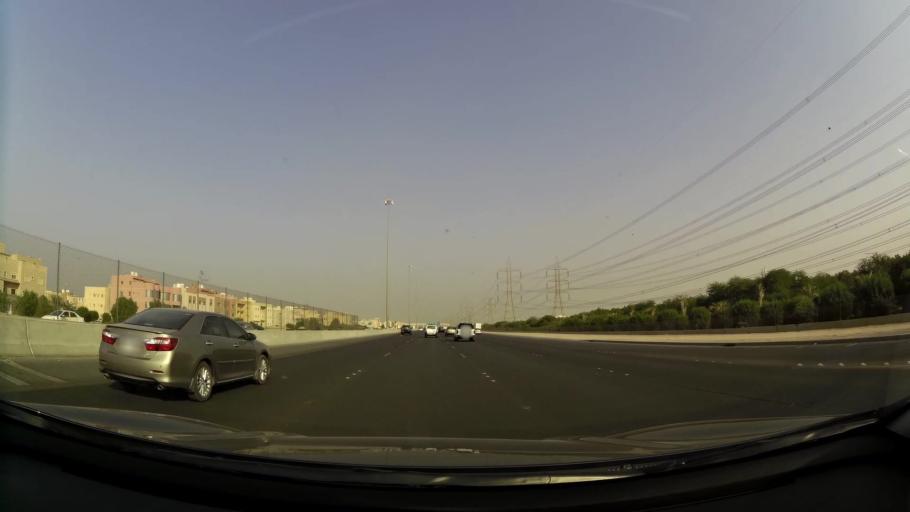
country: KW
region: Al Asimah
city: Ar Rabiyah
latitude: 29.2977
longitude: 47.8935
